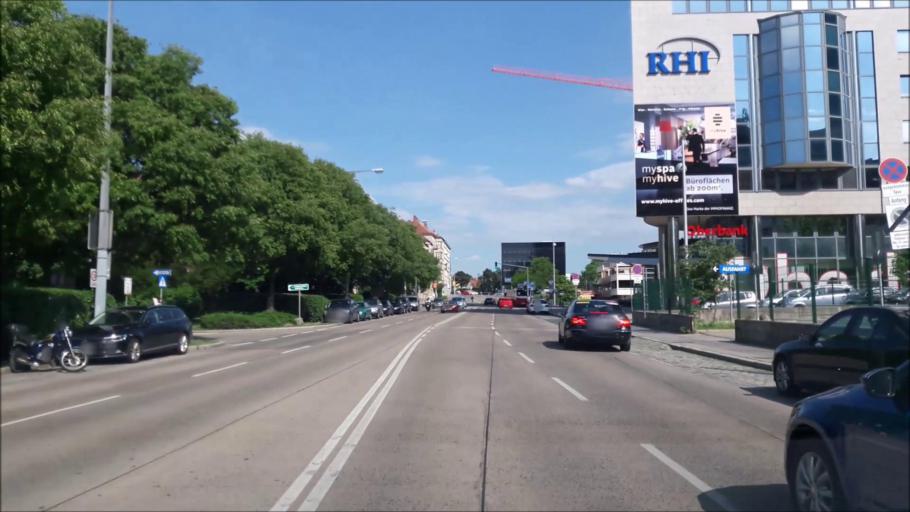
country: AT
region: Vienna
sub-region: Wien Stadt
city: Vienna
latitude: 48.1696
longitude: 16.3460
